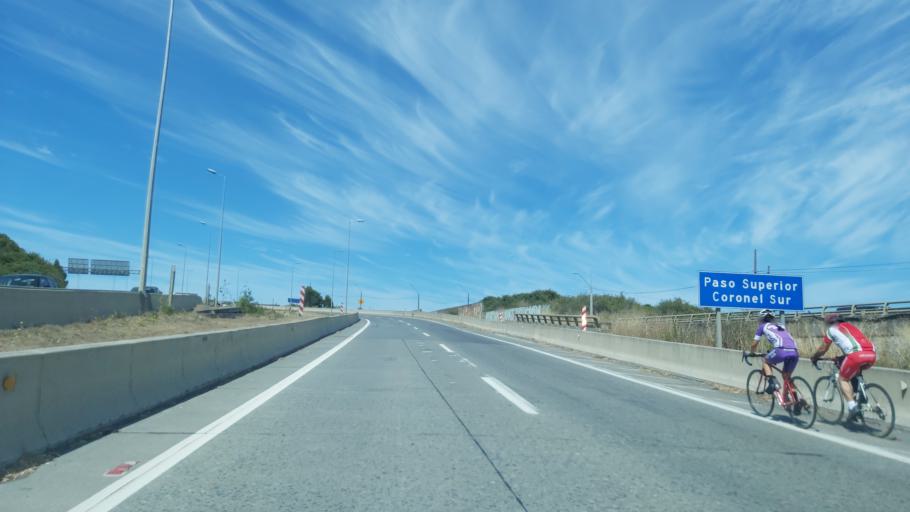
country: CL
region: Biobio
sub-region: Provincia de Concepcion
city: Coronel
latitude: -37.0455
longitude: -73.1414
